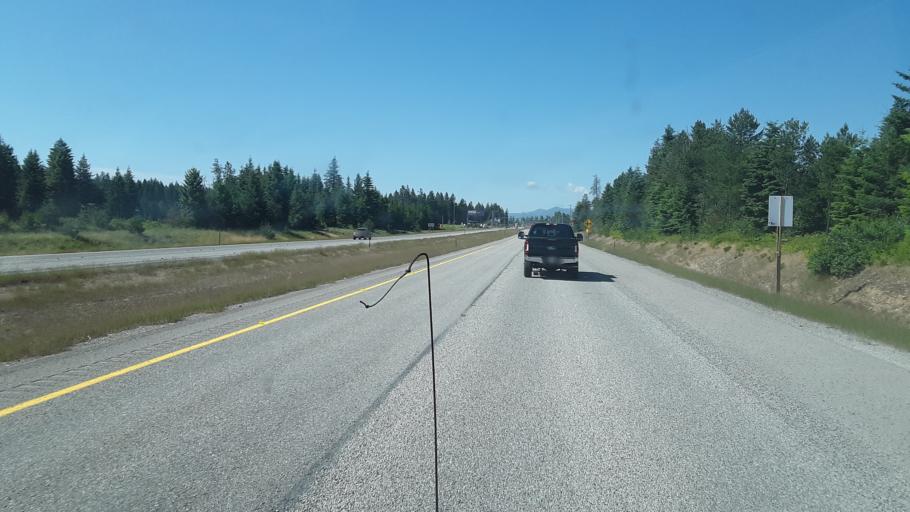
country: US
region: Idaho
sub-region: Kootenai County
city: Hayden
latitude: 47.8358
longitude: -116.7743
